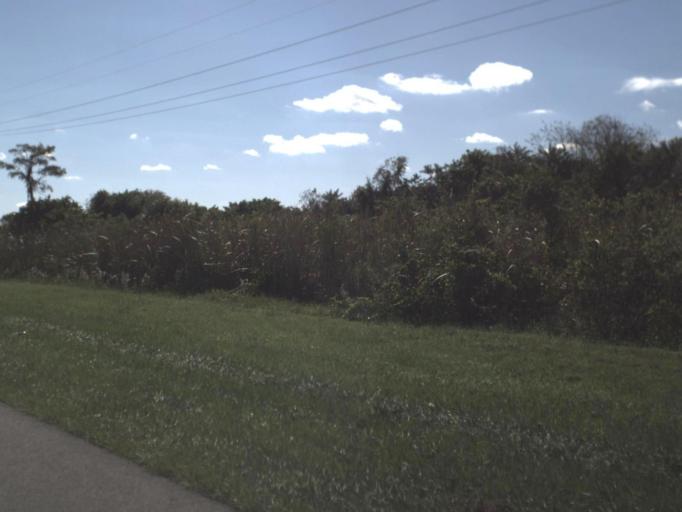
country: US
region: Florida
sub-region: Lee County
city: Lehigh Acres
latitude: 26.5327
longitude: -81.6197
